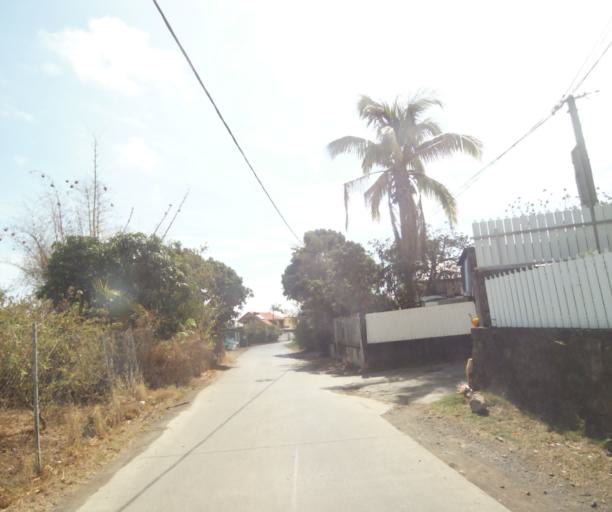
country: RE
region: Reunion
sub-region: Reunion
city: Saint-Paul
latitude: -21.0512
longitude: 55.2652
